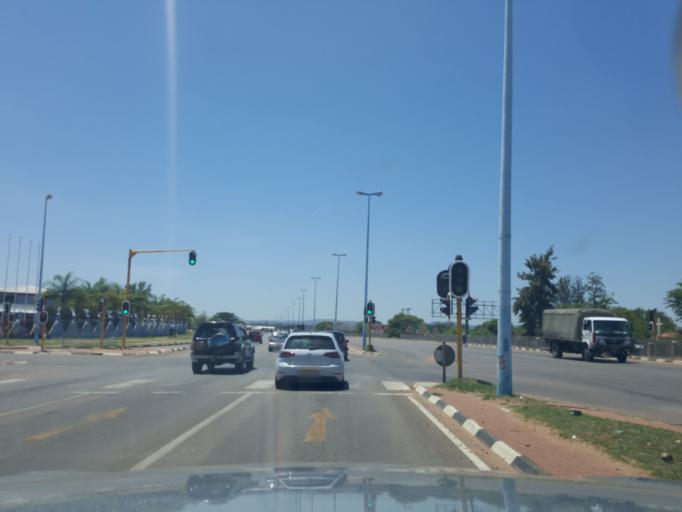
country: BW
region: Kweneng
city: Mogoditshane
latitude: -24.6322
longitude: 25.8741
